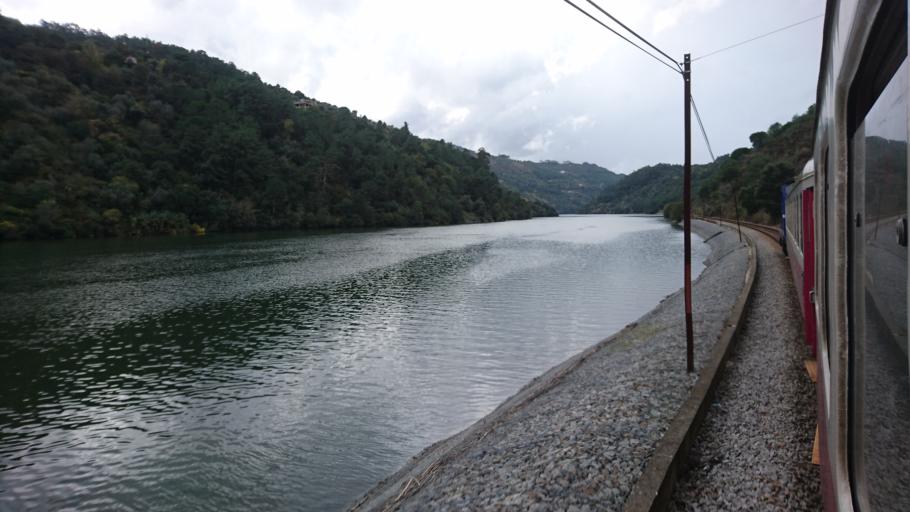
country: PT
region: Viseu
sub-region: Resende
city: Resende
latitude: 41.0979
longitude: -8.0297
